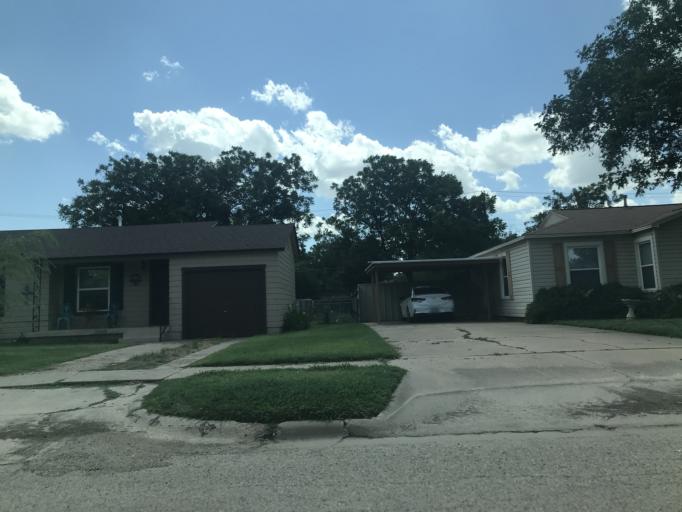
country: US
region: Texas
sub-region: Taylor County
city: Abilene
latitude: 32.4275
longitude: -99.7624
